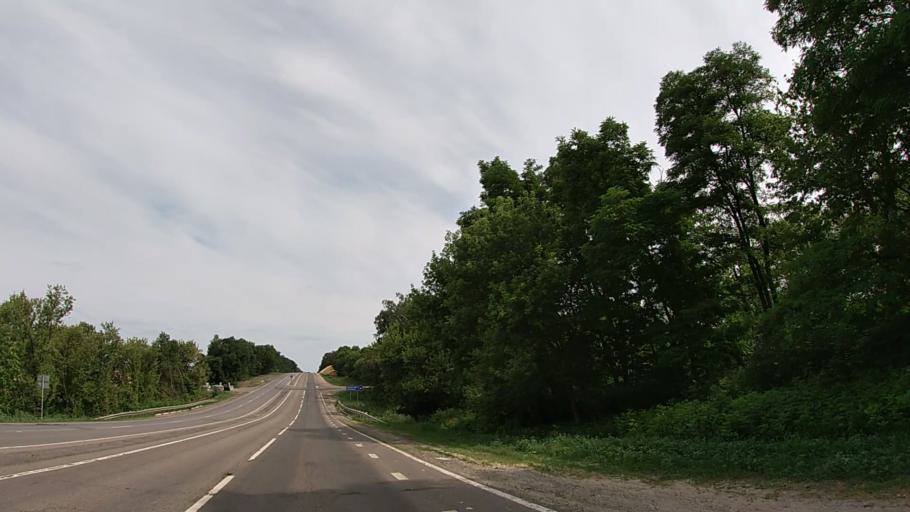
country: RU
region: Belgorod
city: Mayskiy
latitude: 50.4719
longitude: 36.4048
